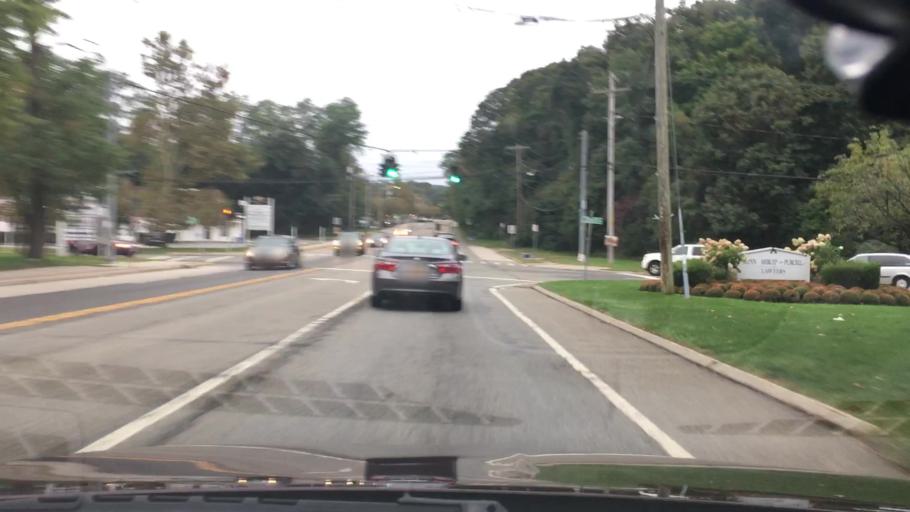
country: US
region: New York
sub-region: Suffolk County
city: Setauket-East Setauket
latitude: 40.9304
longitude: -73.1152
